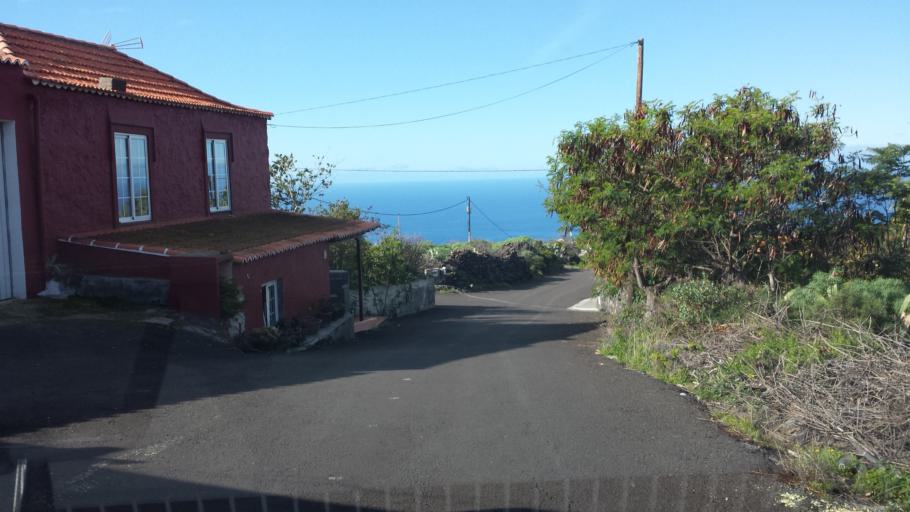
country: ES
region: Canary Islands
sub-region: Provincia de Santa Cruz de Tenerife
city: El Paso
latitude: 28.6114
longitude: -17.8922
